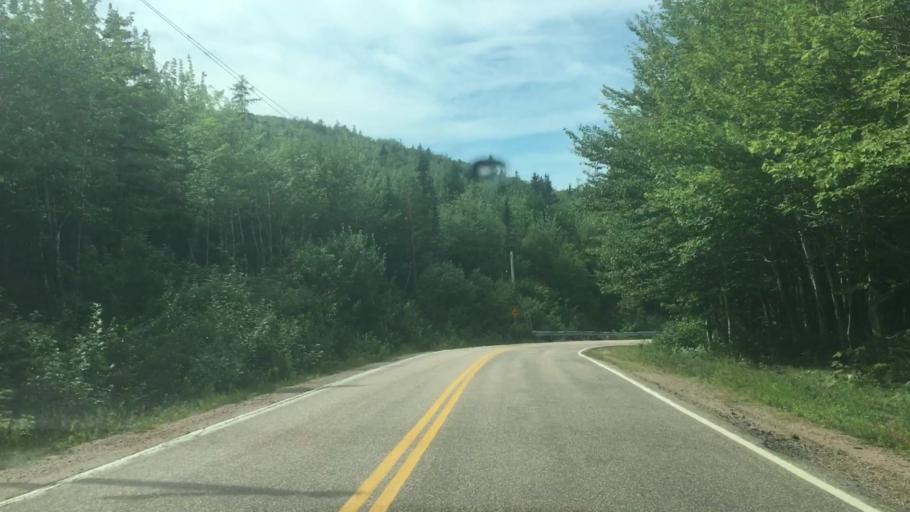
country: CA
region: Nova Scotia
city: Sydney Mines
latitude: 46.6062
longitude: -60.3963
